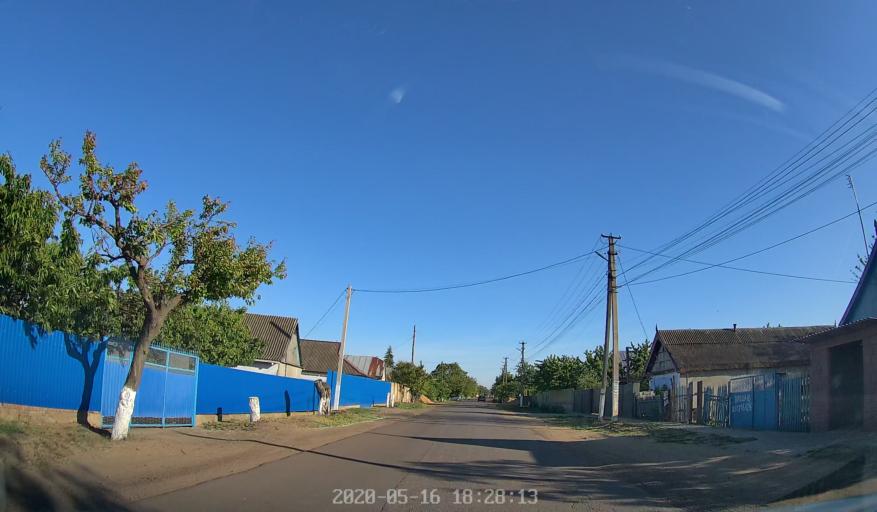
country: MD
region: Telenesti
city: Dnestrovsc
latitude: 46.5417
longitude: 30.0137
